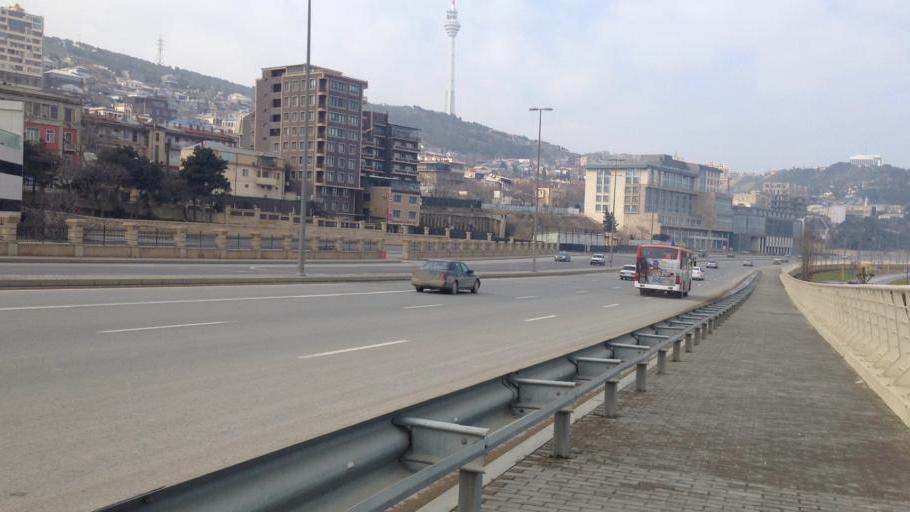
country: AZ
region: Baki
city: Badamdar
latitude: 40.3469
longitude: 49.8394
